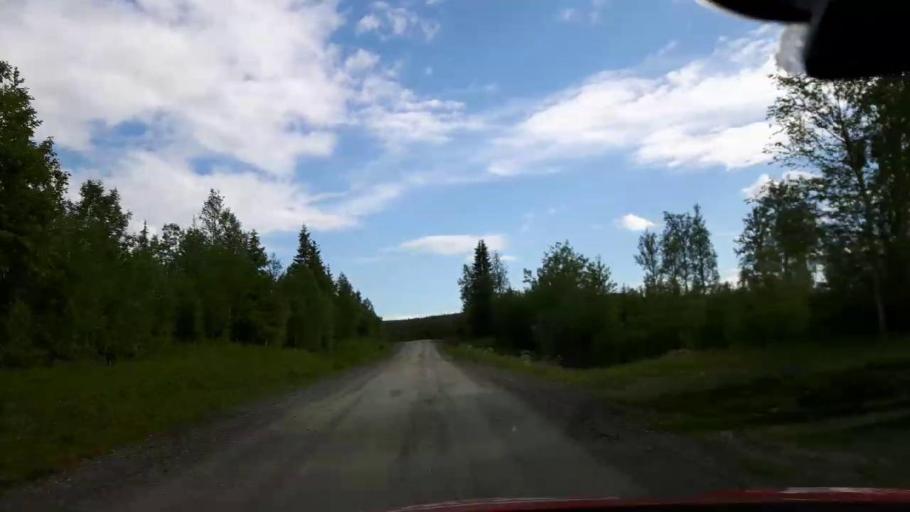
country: SE
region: Jaemtland
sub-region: Krokoms Kommun
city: Valla
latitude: 63.8846
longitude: 14.1481
